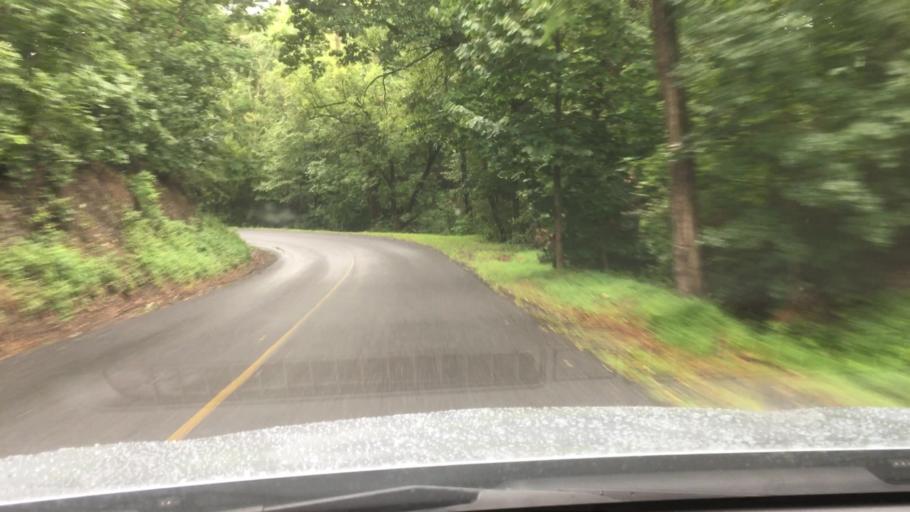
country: US
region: Pennsylvania
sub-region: Franklin County
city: Greencastle
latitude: 39.8701
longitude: -77.7904
